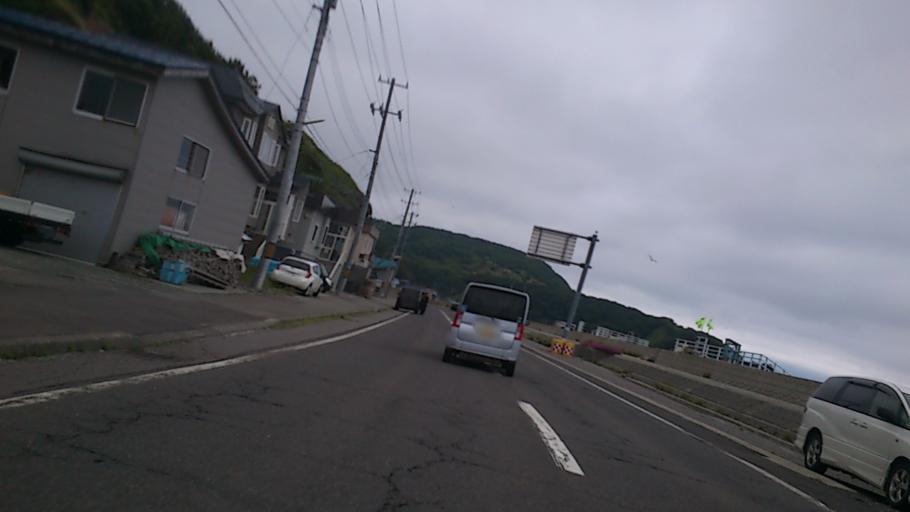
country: JP
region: Hokkaido
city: Iwanai
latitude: 42.7298
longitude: 140.0807
